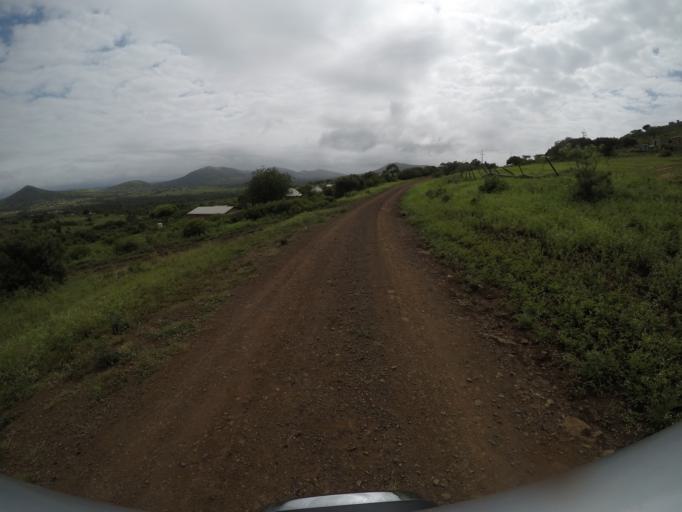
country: ZA
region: KwaZulu-Natal
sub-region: uThungulu District Municipality
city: Empangeni
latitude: -28.6290
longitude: 31.8649
